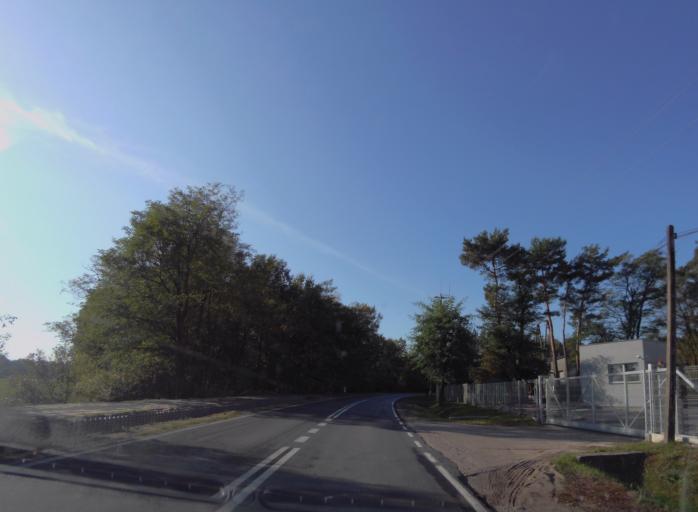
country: PL
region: Masovian Voivodeship
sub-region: Powiat minski
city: Halinow
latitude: 52.1984
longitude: 21.3762
